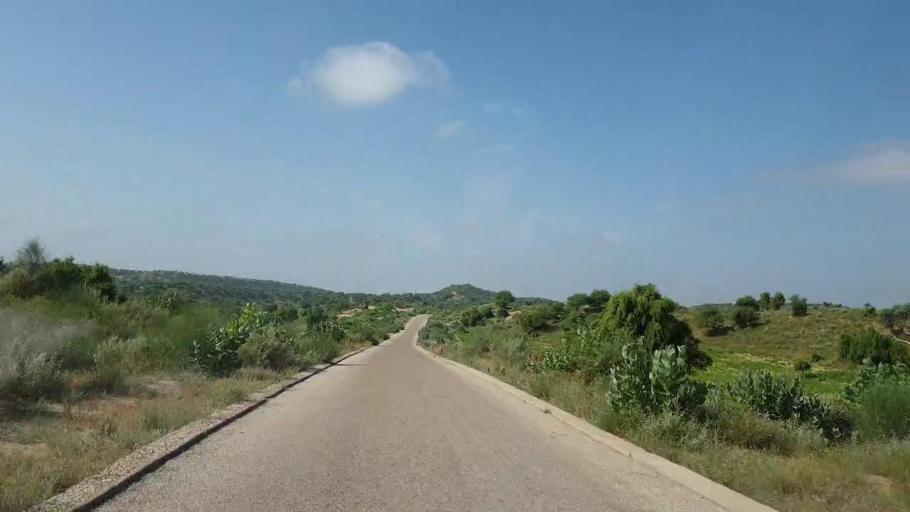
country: PK
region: Sindh
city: Mithi
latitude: 24.5545
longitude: 69.8928
